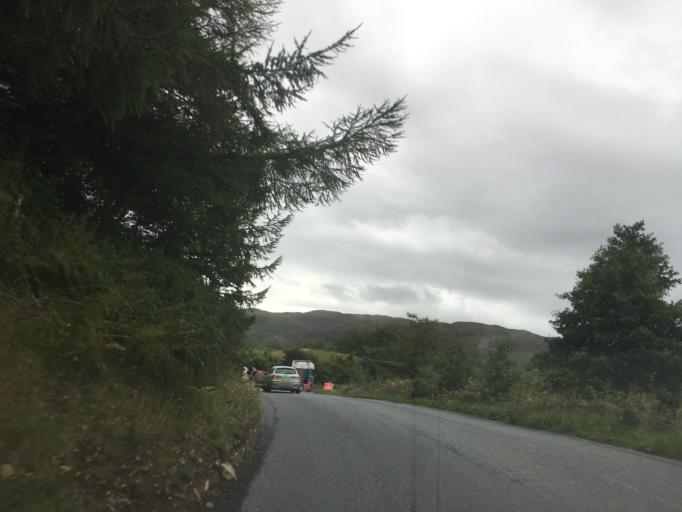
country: GB
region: Scotland
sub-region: Argyll and Bute
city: Oban
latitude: 56.2671
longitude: -5.4796
